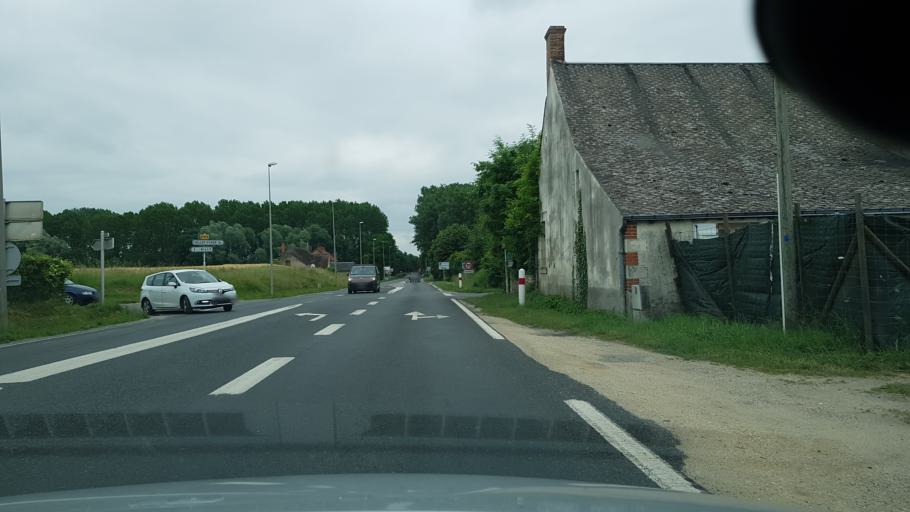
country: FR
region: Centre
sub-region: Departement du Loir-et-Cher
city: Selles-sur-Cher
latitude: 47.2891
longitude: 1.5320
